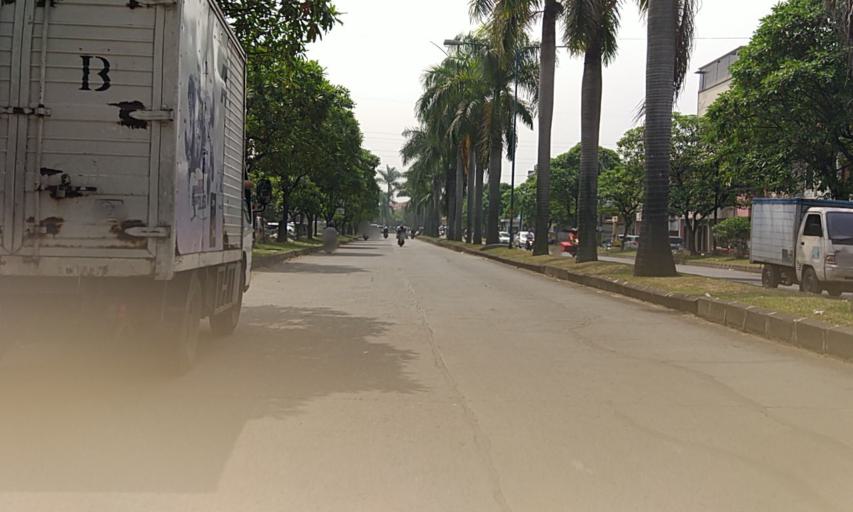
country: ID
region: West Java
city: Margahayukencana
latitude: -6.9595
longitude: 107.5604
